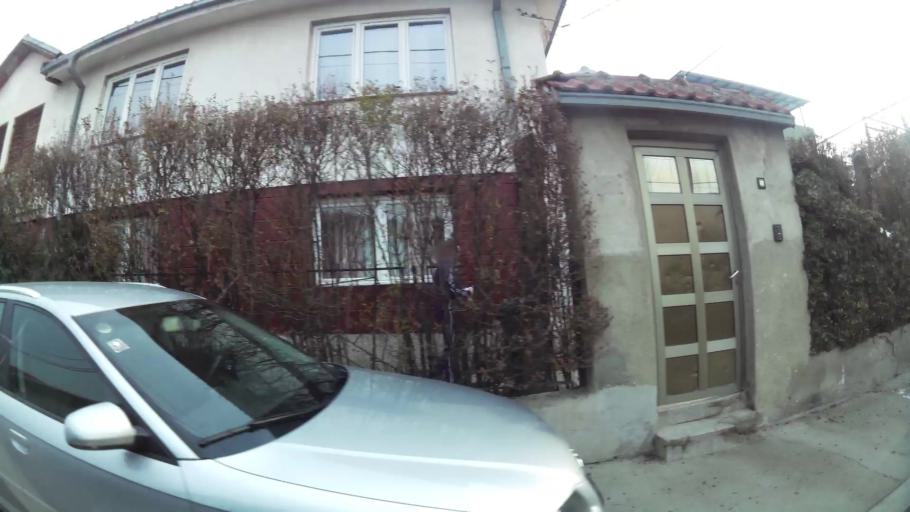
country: MK
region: Cair
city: Cair
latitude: 42.0087
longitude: 21.4468
